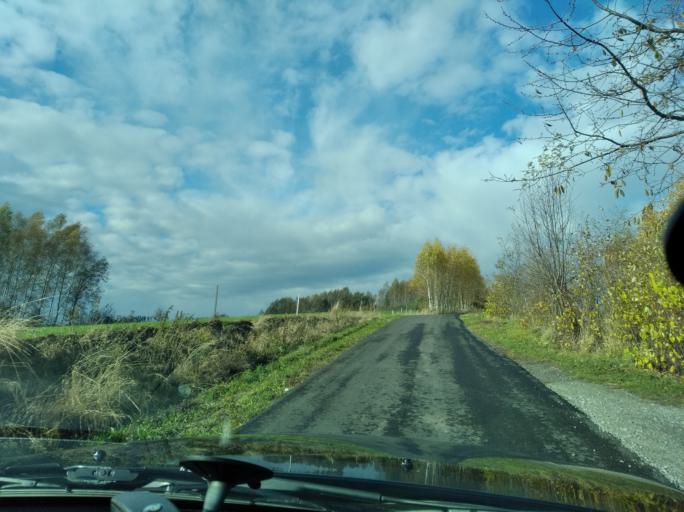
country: PL
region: Subcarpathian Voivodeship
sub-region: Powiat debicki
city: Debica
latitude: 50.0252
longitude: 21.4685
